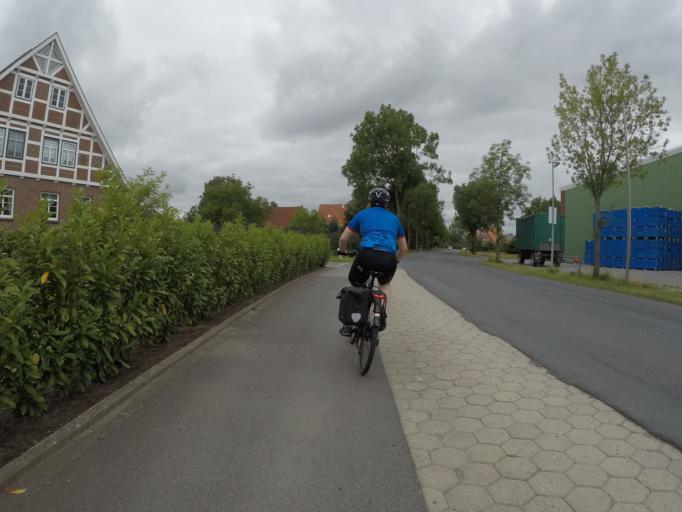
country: DE
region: Lower Saxony
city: Grunendeich
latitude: 53.5733
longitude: 9.6046
